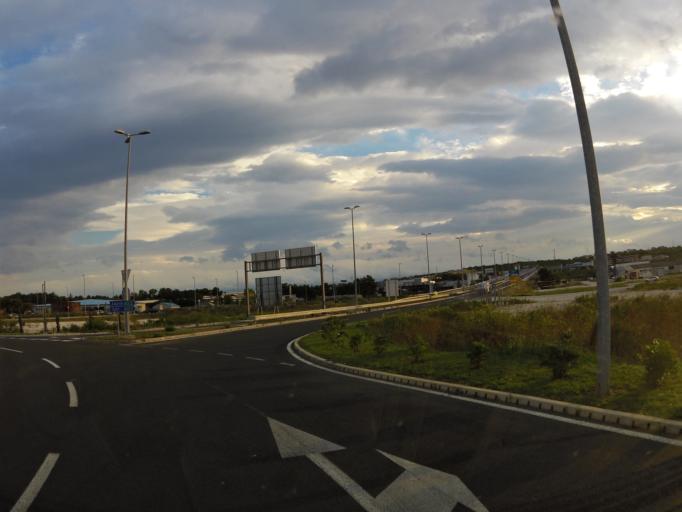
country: HR
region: Zadarska
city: Zadar
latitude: 44.0920
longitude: 15.2630
